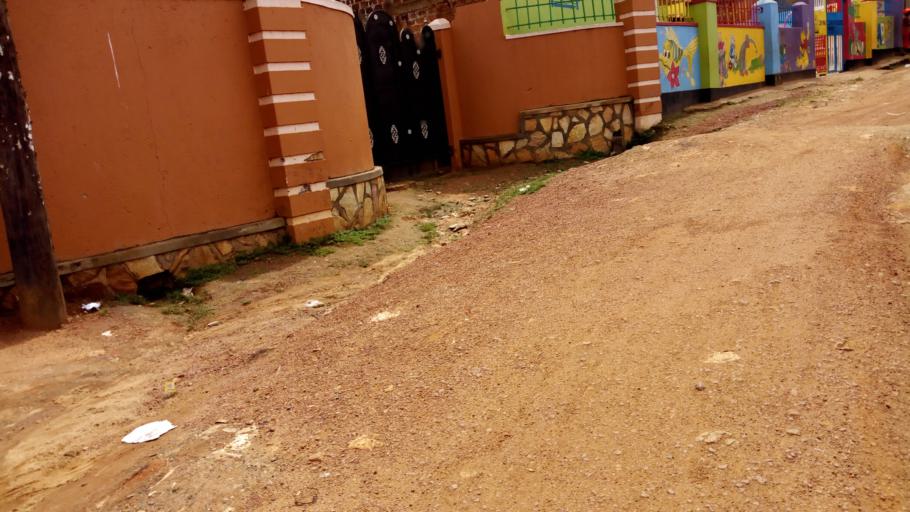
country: UG
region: Central Region
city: Kampala Central Division
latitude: 0.3765
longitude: 32.5619
